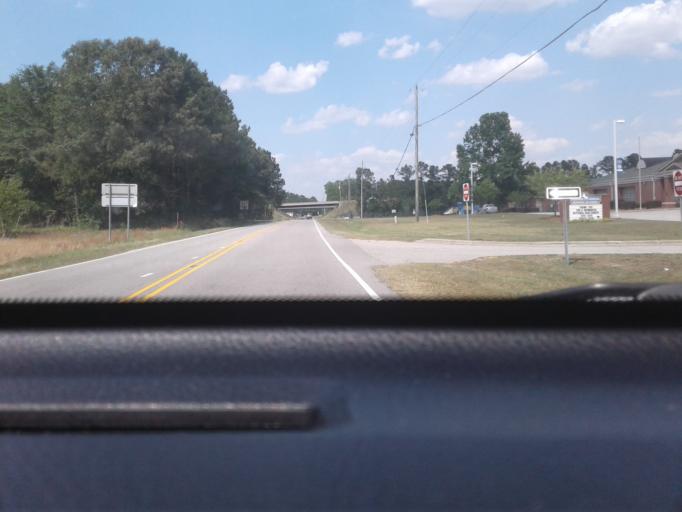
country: US
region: North Carolina
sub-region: Cumberland County
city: Eastover
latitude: 35.1226
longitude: -78.7627
